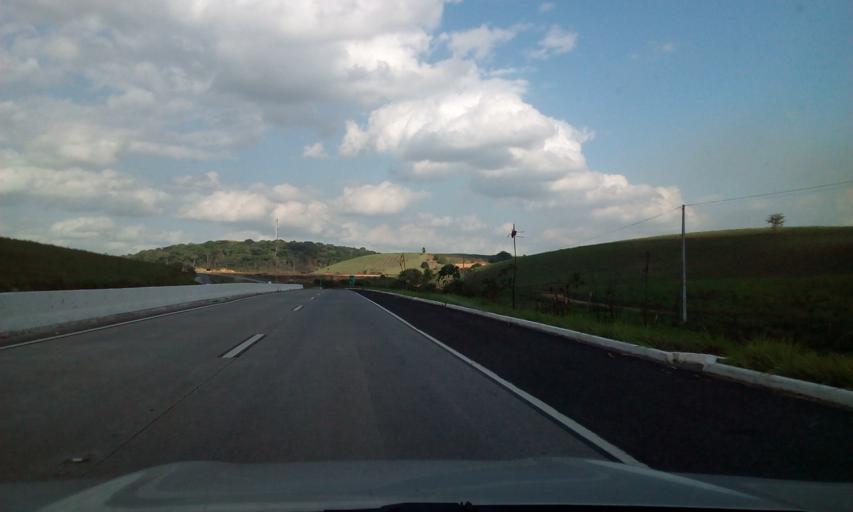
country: BR
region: Pernambuco
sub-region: Joaquim Nabuco
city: Joaquim Nabuco
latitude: -8.5888
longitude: -35.5081
